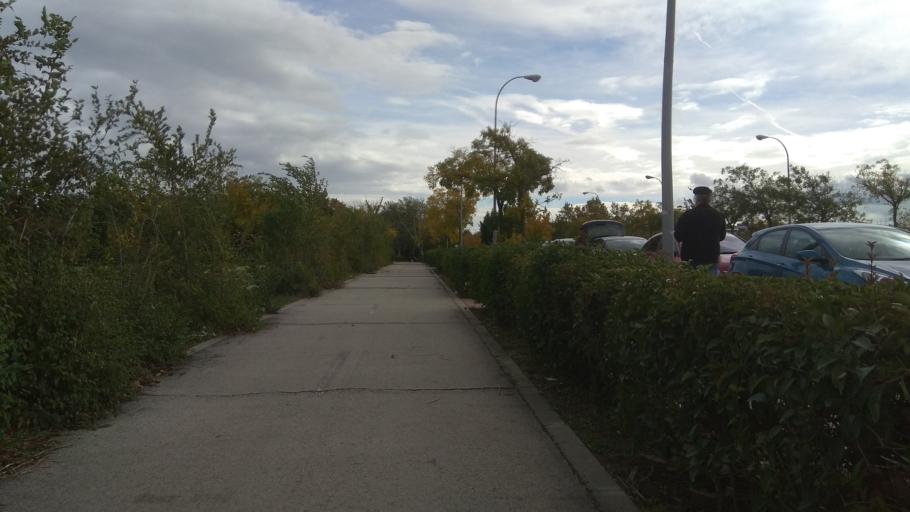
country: ES
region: Madrid
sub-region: Provincia de Madrid
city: Vicalvaro
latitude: 40.4096
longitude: -3.6171
